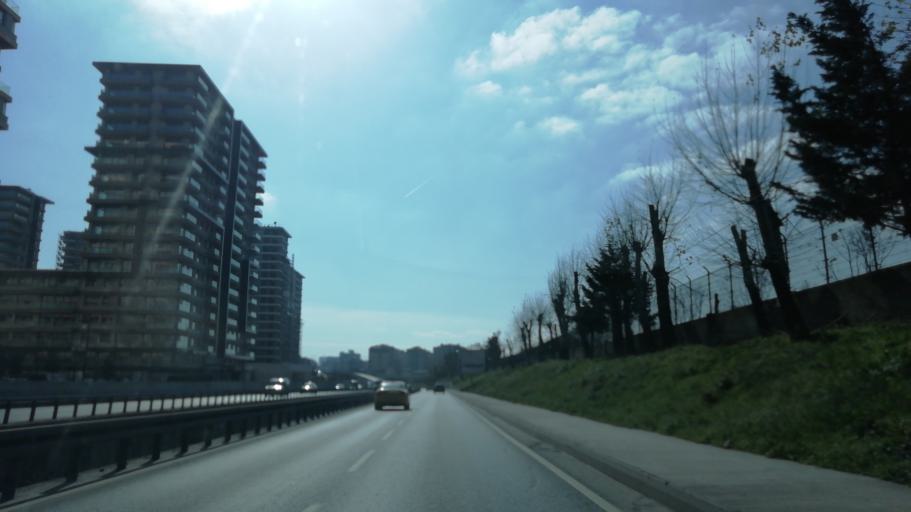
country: TR
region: Istanbul
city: merter keresteciler
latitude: 41.0255
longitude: 28.8992
